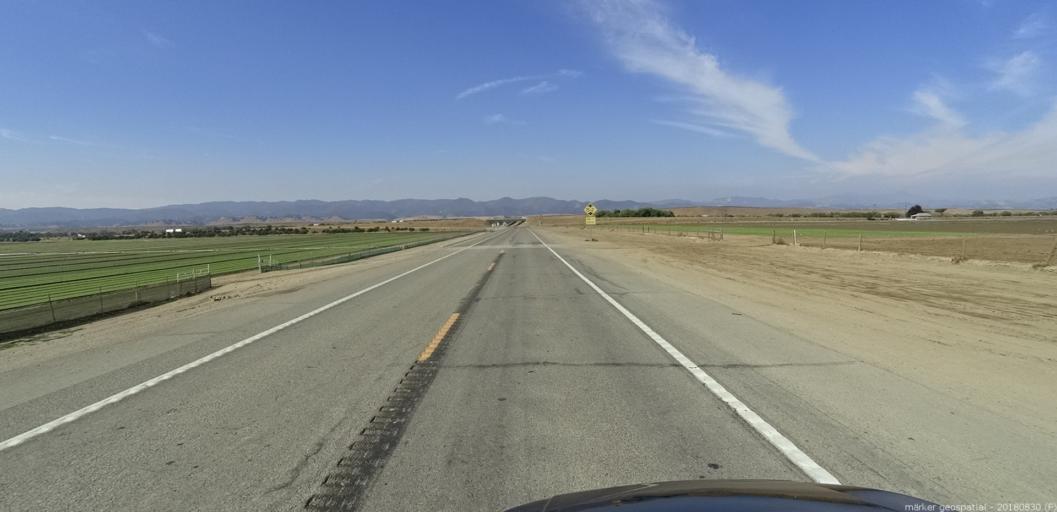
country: US
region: California
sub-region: Monterey County
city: King City
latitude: 36.1244
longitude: -121.0187
